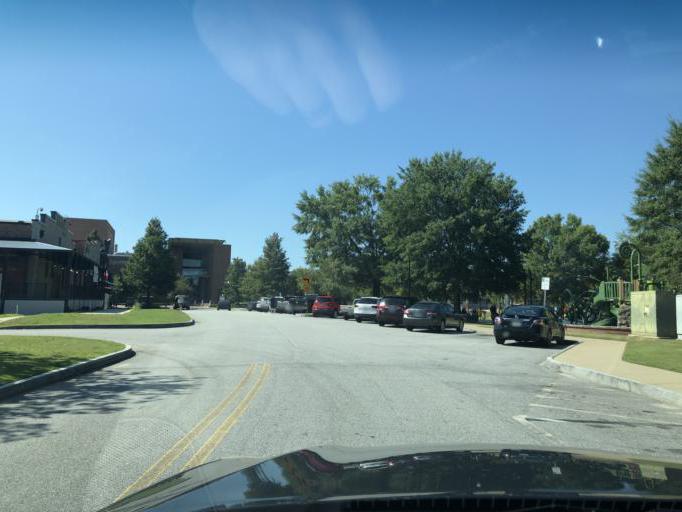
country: US
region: Alabama
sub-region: Russell County
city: Phenix City
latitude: 32.4658
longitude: -84.9959
